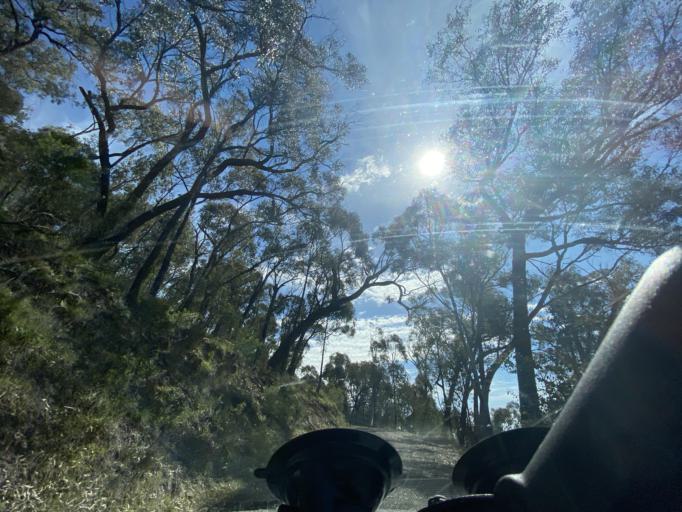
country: AU
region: Victoria
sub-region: Mansfield
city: Mansfield
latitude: -36.8082
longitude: 146.1043
